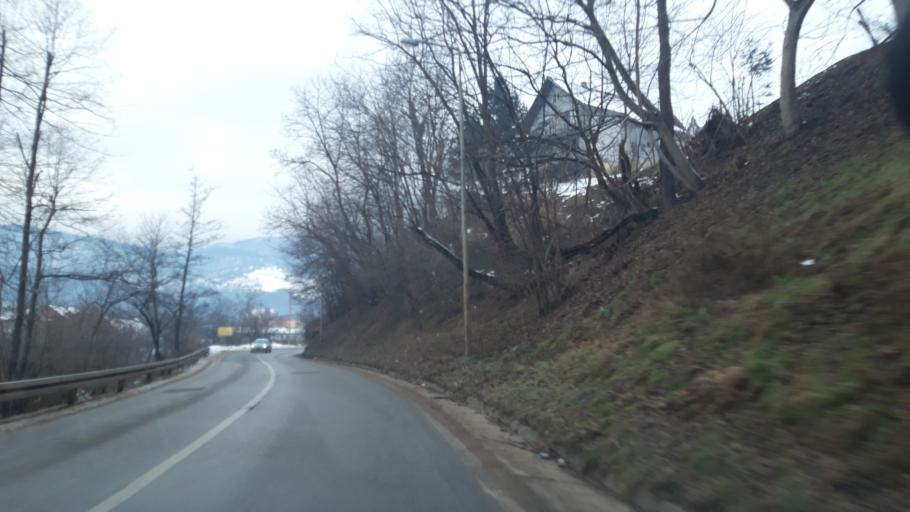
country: BA
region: Republika Srpska
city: Milici
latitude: 44.1673
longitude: 19.0730
